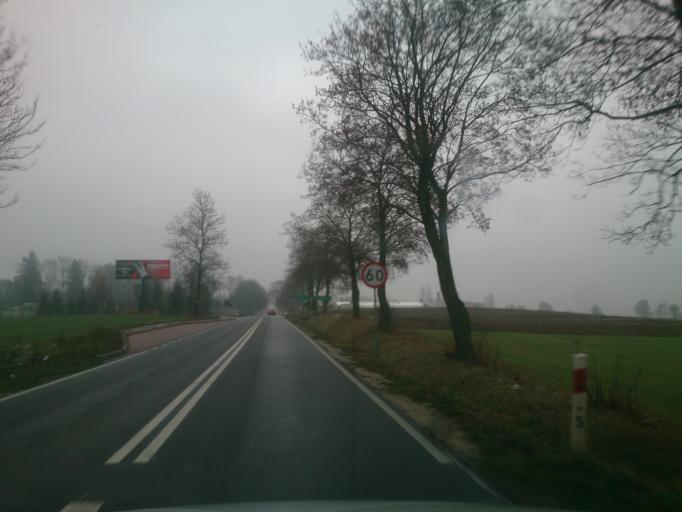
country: PL
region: Kujawsko-Pomorskie
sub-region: Powiat rypinski
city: Rypin
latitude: 53.0998
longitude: 19.3953
